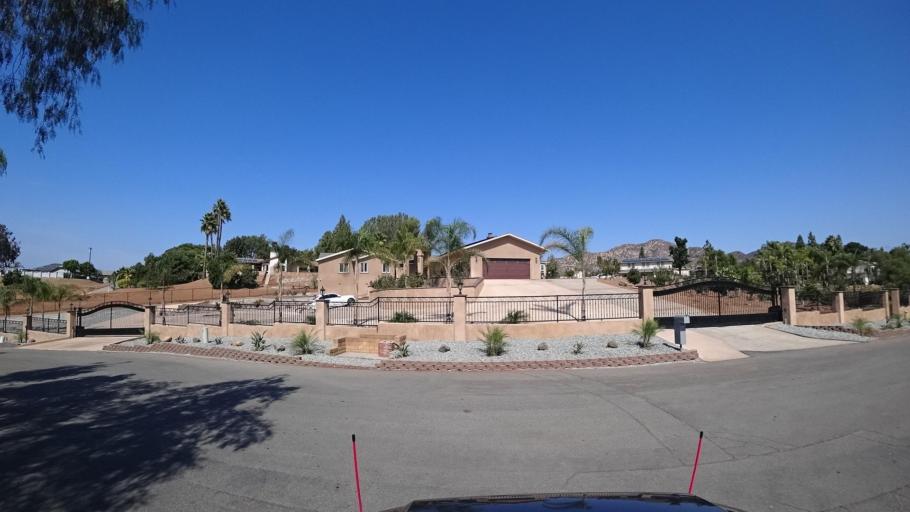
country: US
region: California
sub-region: San Diego County
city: Granite Hills
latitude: 32.7837
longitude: -116.8971
